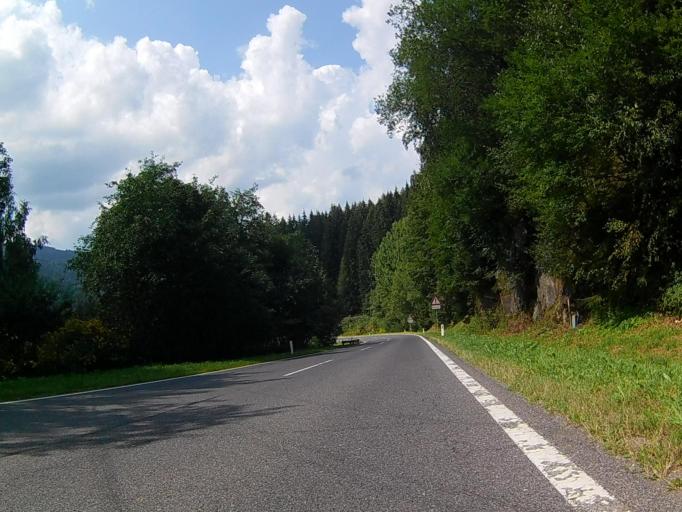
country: AT
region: Styria
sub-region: Politischer Bezirk Deutschlandsberg
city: Soboth
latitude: 46.7077
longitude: 15.0977
